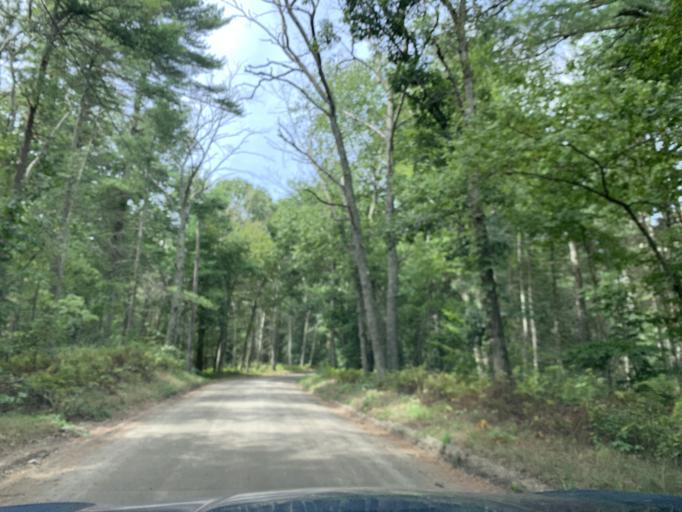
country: US
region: Rhode Island
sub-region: Kent County
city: West Greenwich
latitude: 41.5783
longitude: -71.6467
